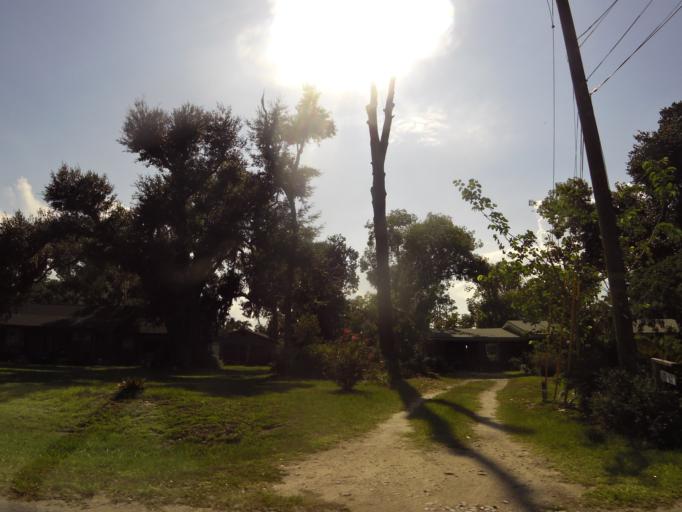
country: US
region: Florida
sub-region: Nassau County
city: Fernandina Beach
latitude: 30.6429
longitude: -81.4629
